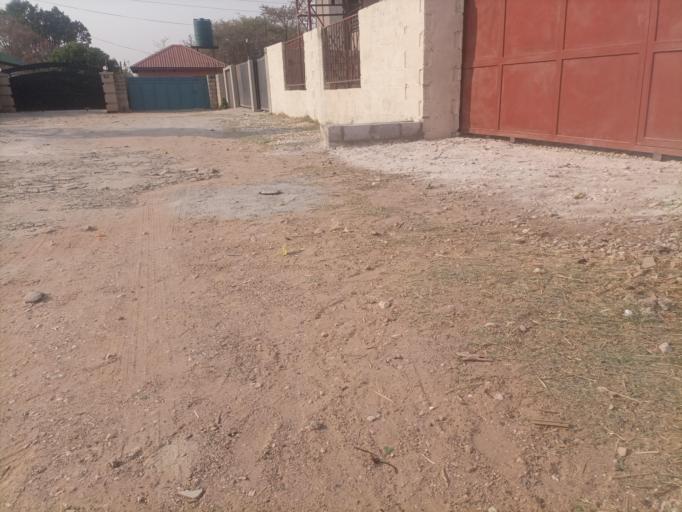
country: ZM
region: Lusaka
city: Lusaka
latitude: -15.4006
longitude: 28.3869
